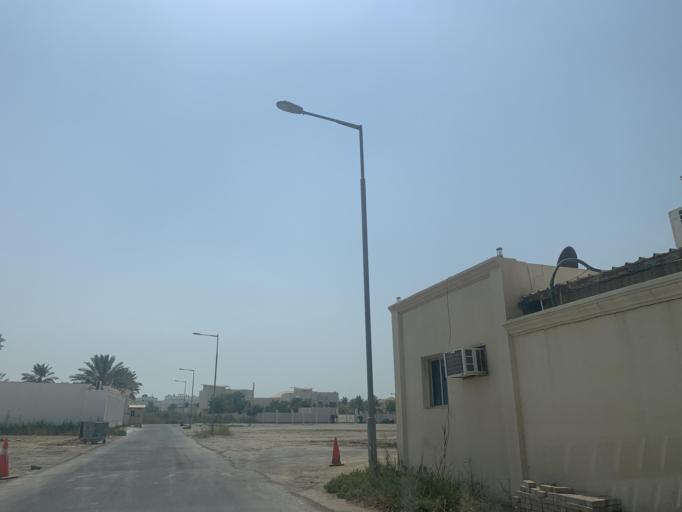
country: BH
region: Manama
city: Jidd Hafs
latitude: 26.1962
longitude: 50.4969
